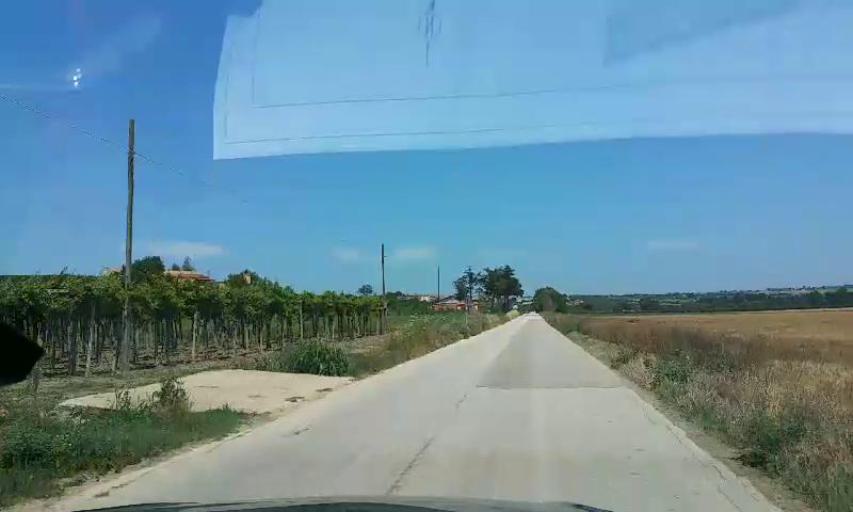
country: IT
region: Molise
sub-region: Provincia di Campobasso
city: San Giacomo degli Schiavoni
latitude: 41.9660
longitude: 14.9005
